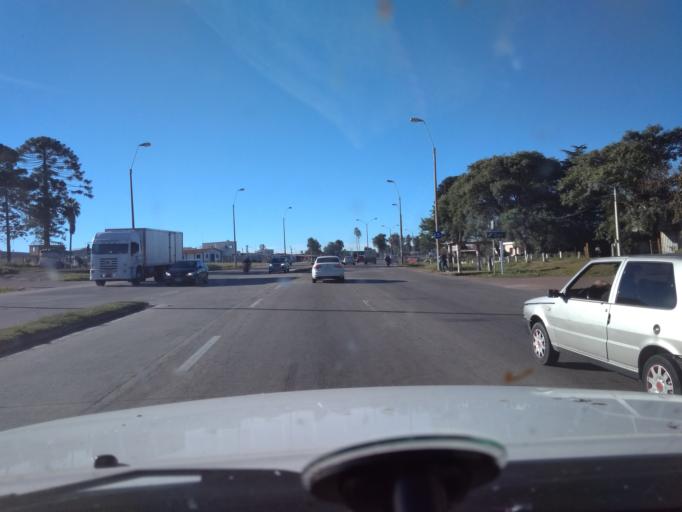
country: UY
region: Canelones
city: Colonia Nicolich
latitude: -34.7819
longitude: -56.0603
